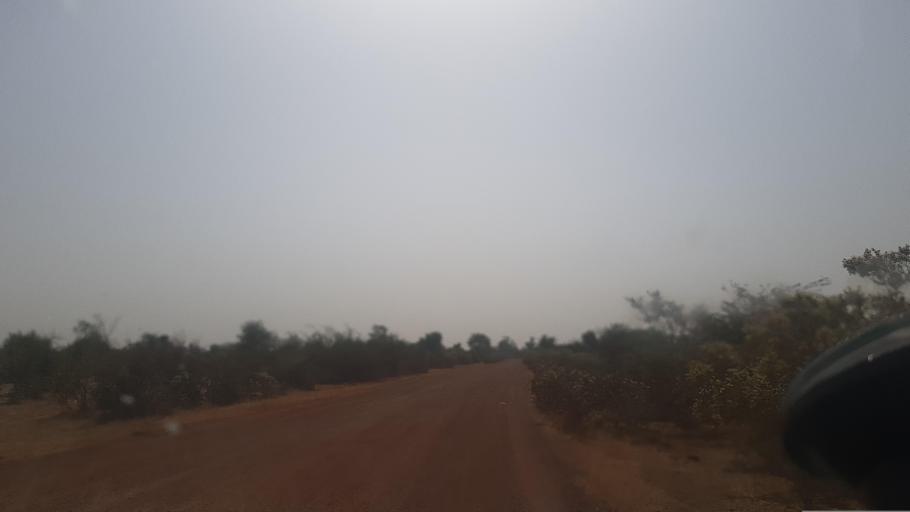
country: ML
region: Segou
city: Baroueli
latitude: 13.0612
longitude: -6.4732
